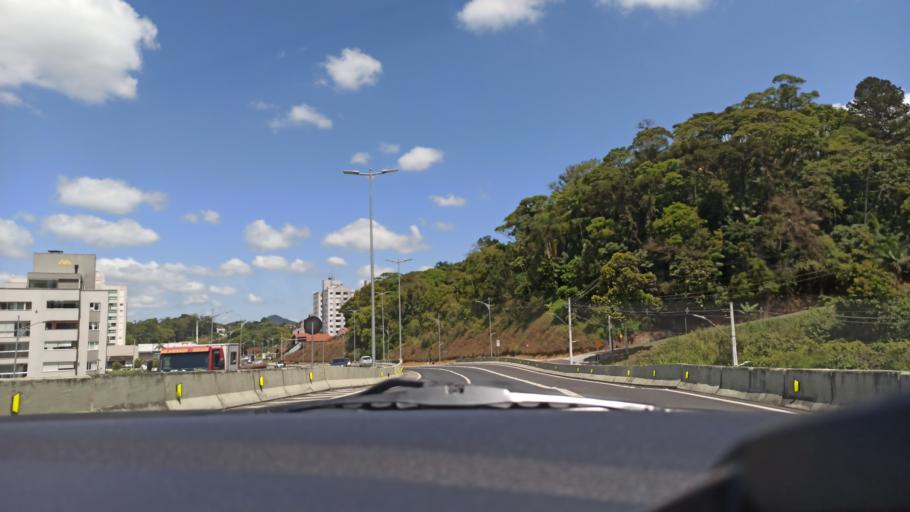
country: BR
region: Santa Catarina
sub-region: Blumenau
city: Blumenau
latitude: -26.9153
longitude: -49.0951
